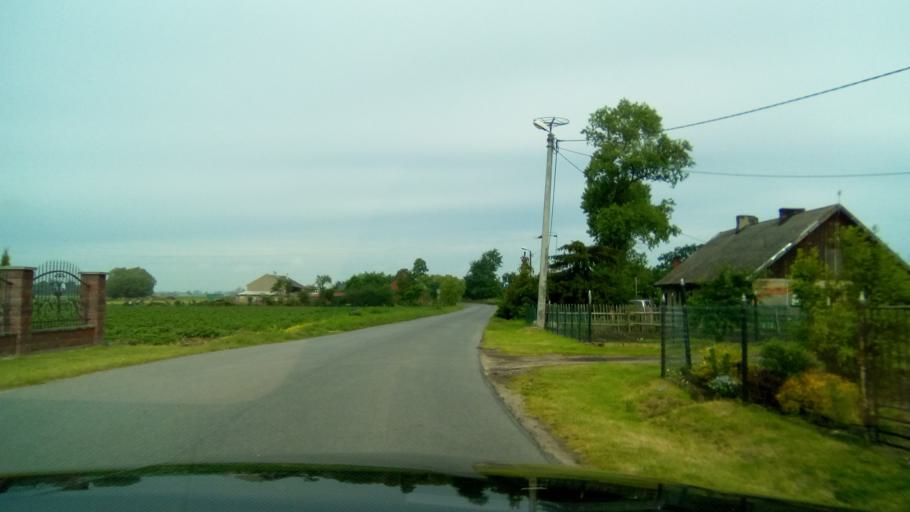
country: PL
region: Greater Poland Voivodeship
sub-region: Powiat gnieznienski
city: Mieleszyn
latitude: 52.6919
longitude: 17.5194
